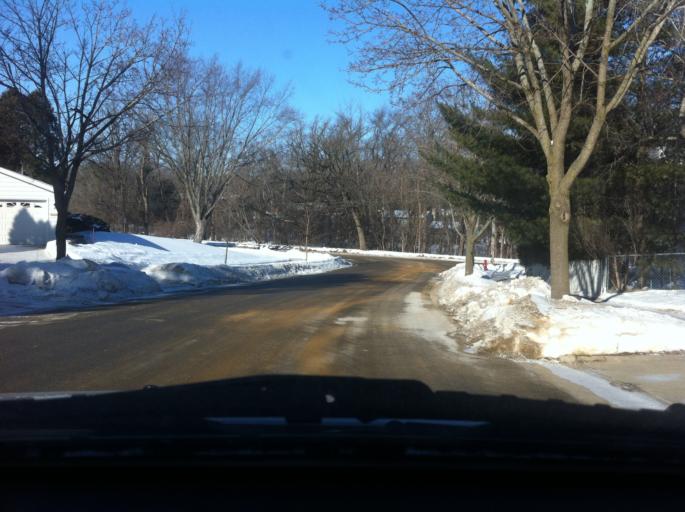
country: US
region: Wisconsin
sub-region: Dane County
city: Middleton
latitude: 43.0633
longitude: -89.4836
